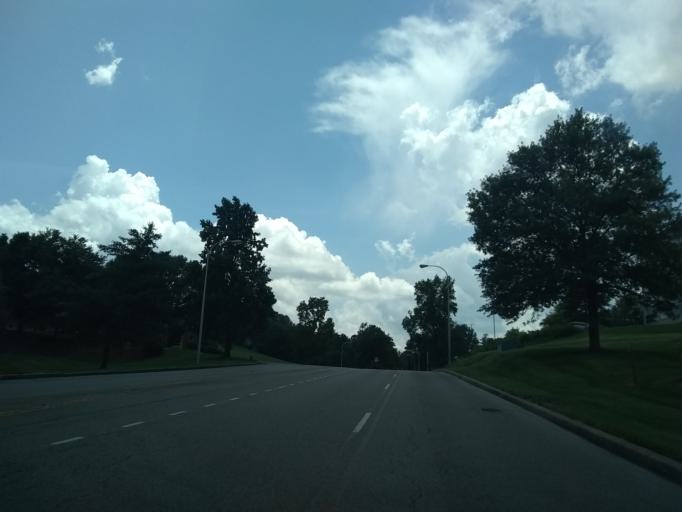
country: US
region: Tennessee
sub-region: Davidson County
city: Nashville
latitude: 36.1473
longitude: -86.6842
